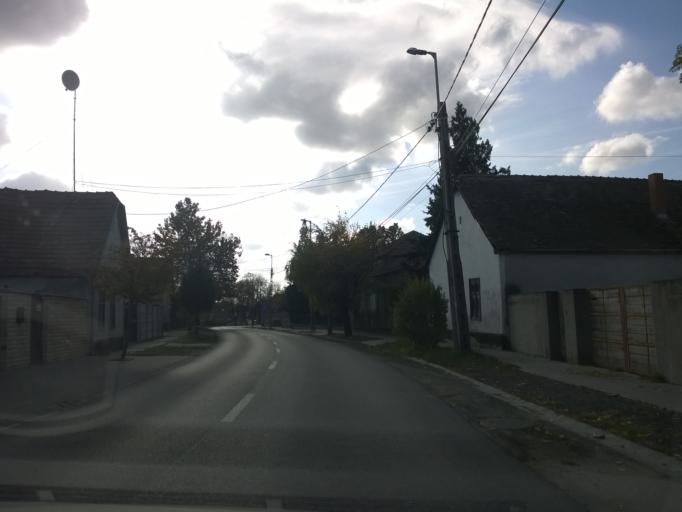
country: HU
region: Pest
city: Rackeve
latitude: 47.1538
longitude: 18.9448
